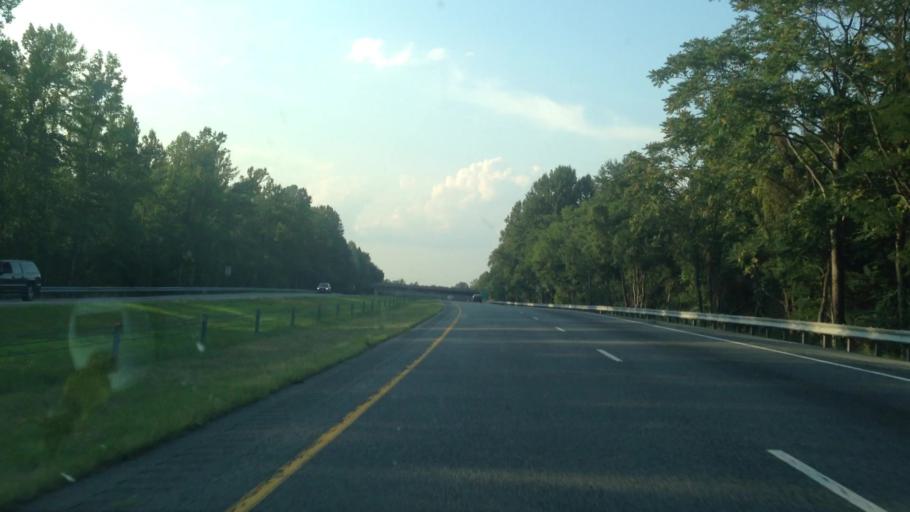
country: US
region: North Carolina
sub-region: Rockingham County
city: Reidsville
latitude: 36.4300
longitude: -79.5725
